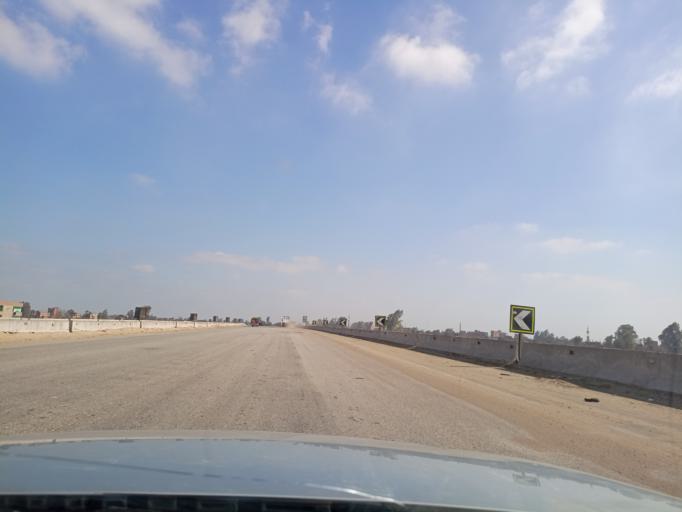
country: EG
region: Muhafazat al Minufiyah
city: Al Bajur
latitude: 30.4206
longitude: 31.0824
